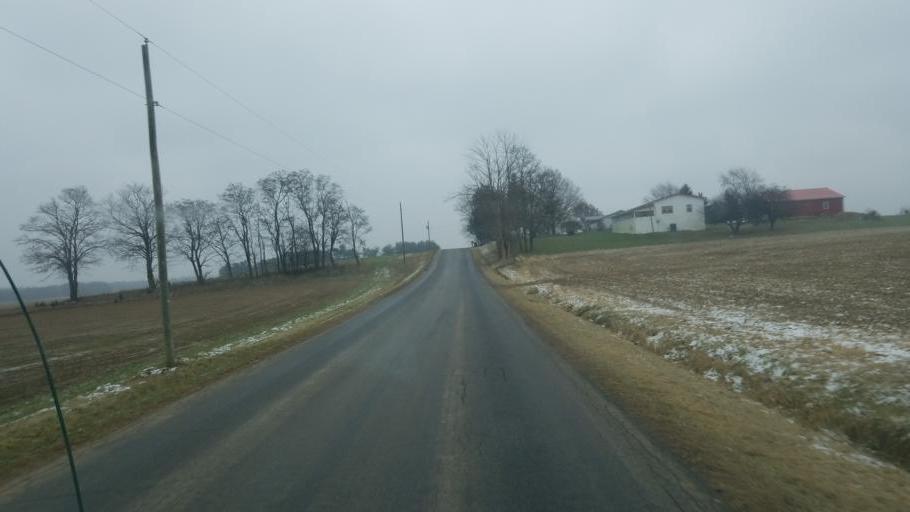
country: US
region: Ohio
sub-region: Huron County
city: Greenwich
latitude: 40.9754
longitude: -82.5474
